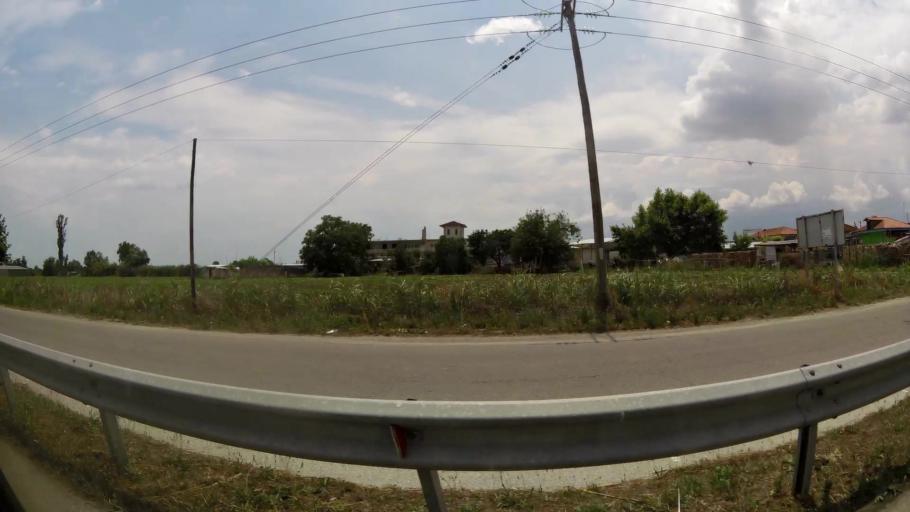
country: GR
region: Central Macedonia
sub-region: Nomos Pierias
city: Kallithea
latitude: 40.2708
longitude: 22.5696
